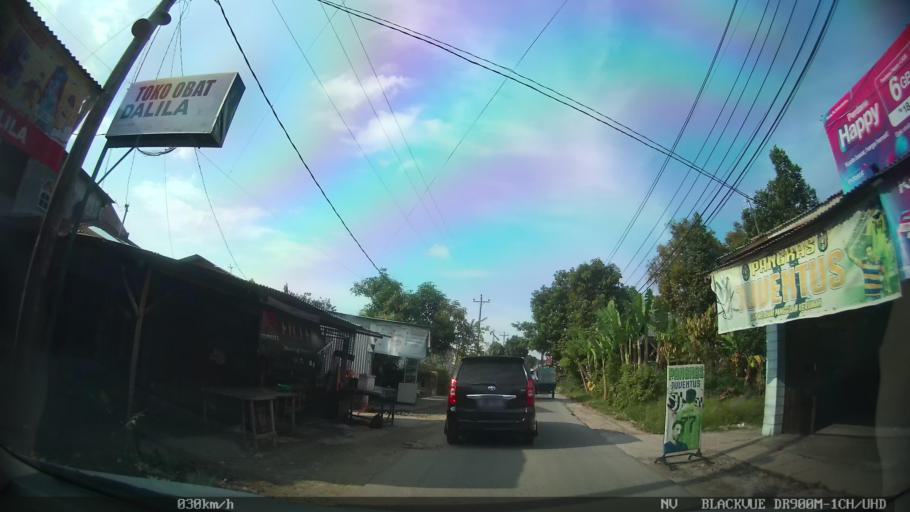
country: ID
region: North Sumatra
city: Medan
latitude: 3.6028
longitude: 98.7419
